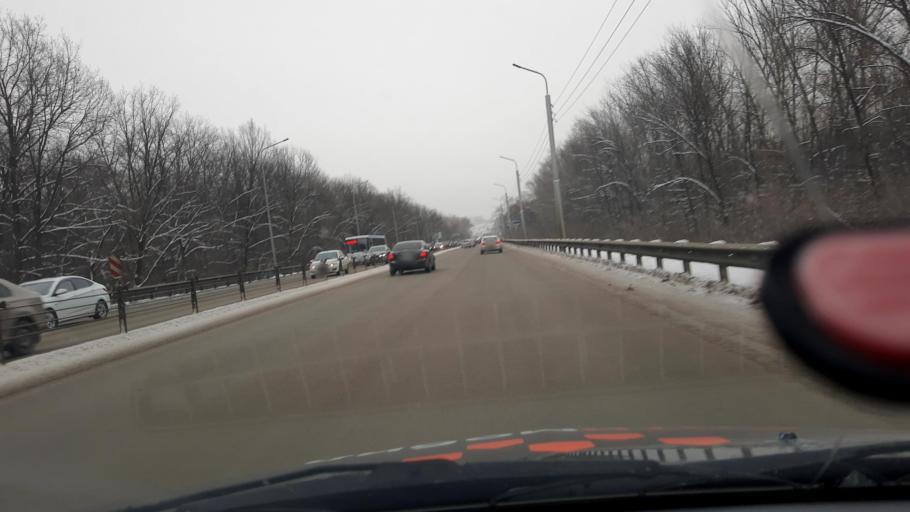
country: RU
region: Bashkortostan
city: Ufa
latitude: 54.7001
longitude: 55.9235
